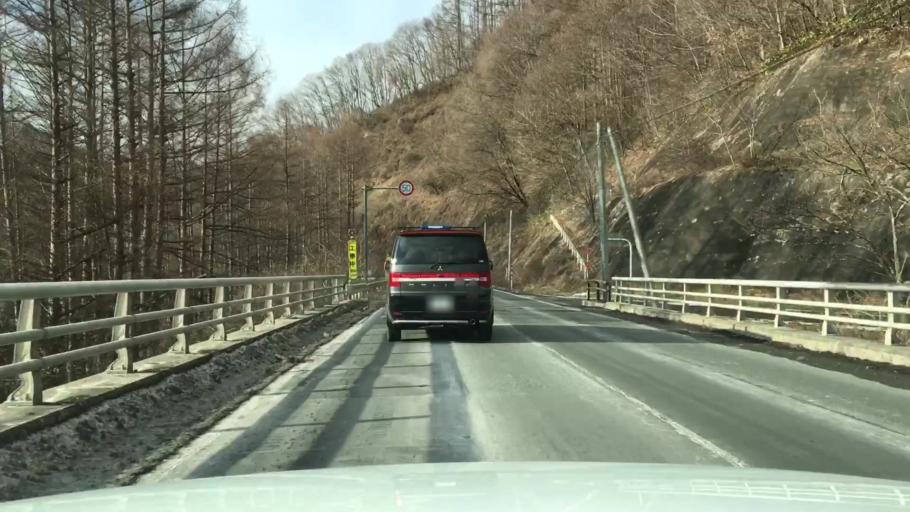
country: JP
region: Iwate
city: Morioka-shi
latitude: 39.6673
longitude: 141.3009
